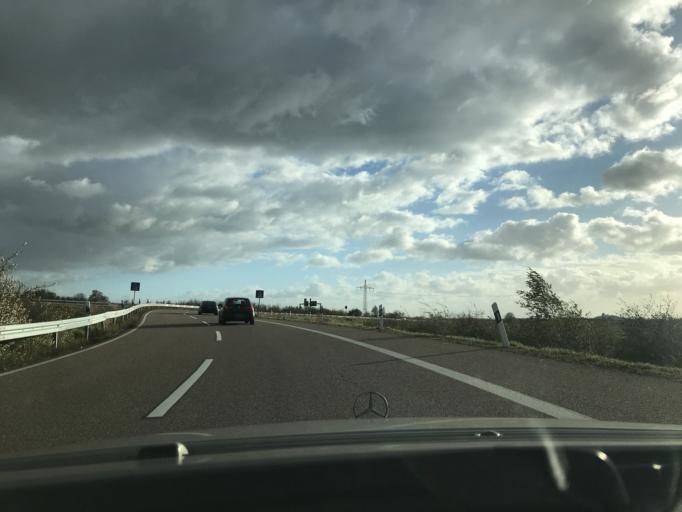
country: DE
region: Saxony-Anhalt
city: Brehna
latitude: 51.5546
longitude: 12.1849
